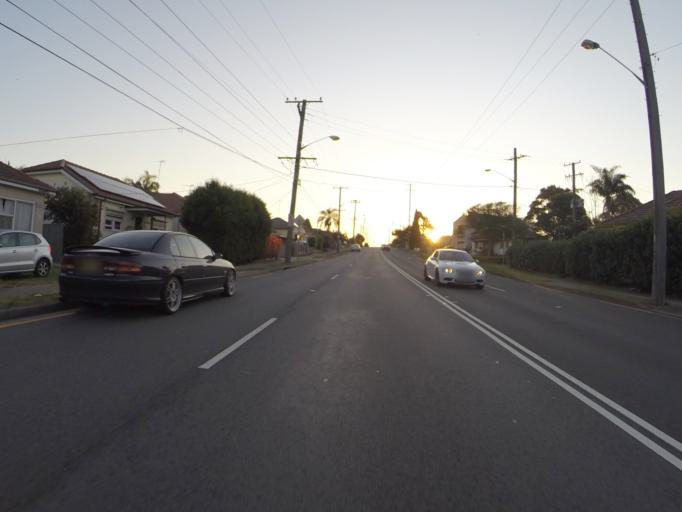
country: AU
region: New South Wales
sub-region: Hurstville
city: Penshurst
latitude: -33.9572
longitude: 151.0752
